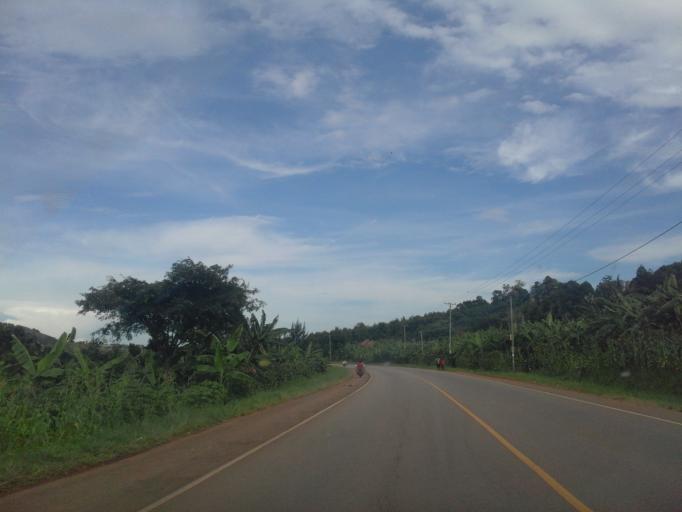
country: UG
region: Central Region
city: Masaka
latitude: -0.3425
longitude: 31.6329
